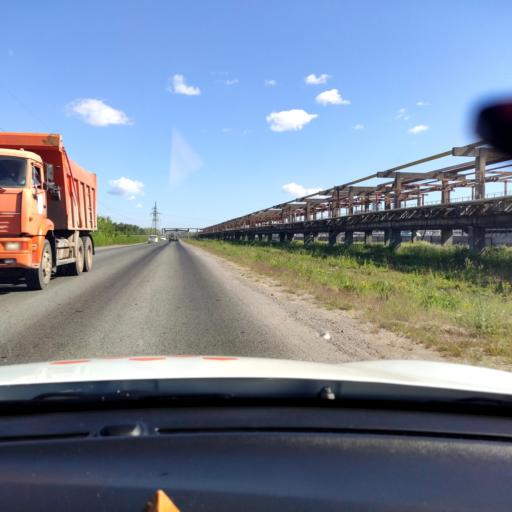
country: RU
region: Tatarstan
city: Staroye Arakchino
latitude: 55.8729
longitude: 48.9746
